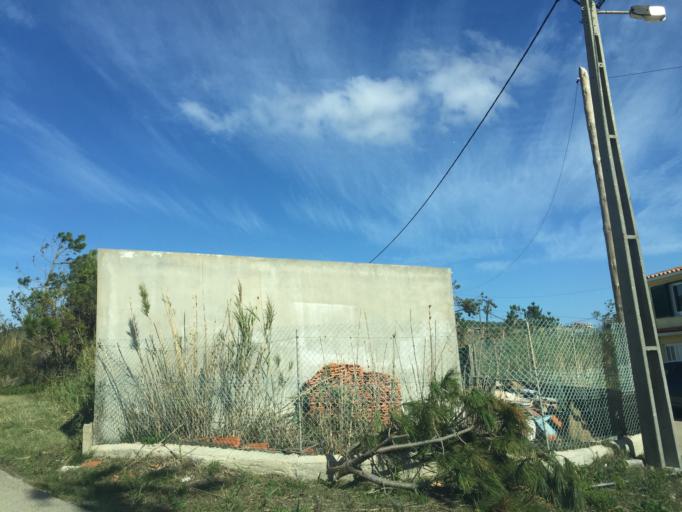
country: PT
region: Coimbra
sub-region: Figueira da Foz
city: Buarcos
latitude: 40.1814
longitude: -8.9049
